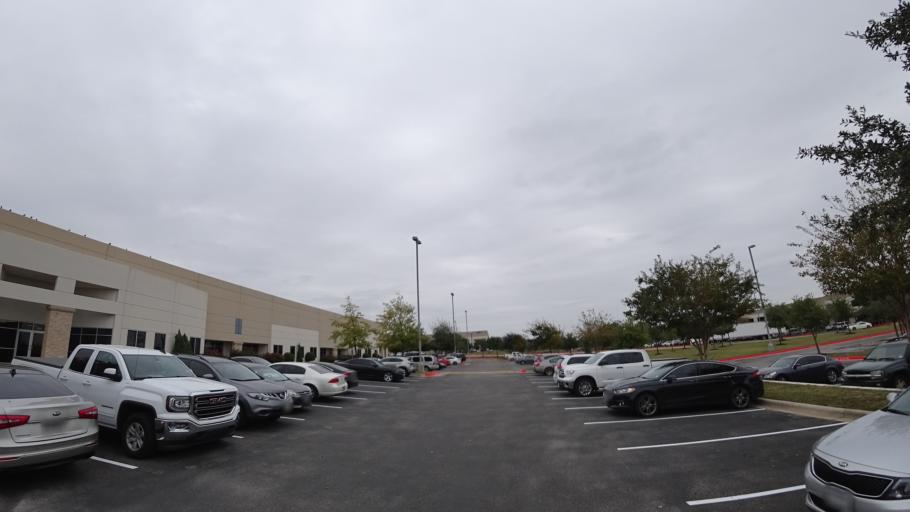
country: US
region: Texas
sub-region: Travis County
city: Wells Branch
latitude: 30.4473
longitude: -97.7091
